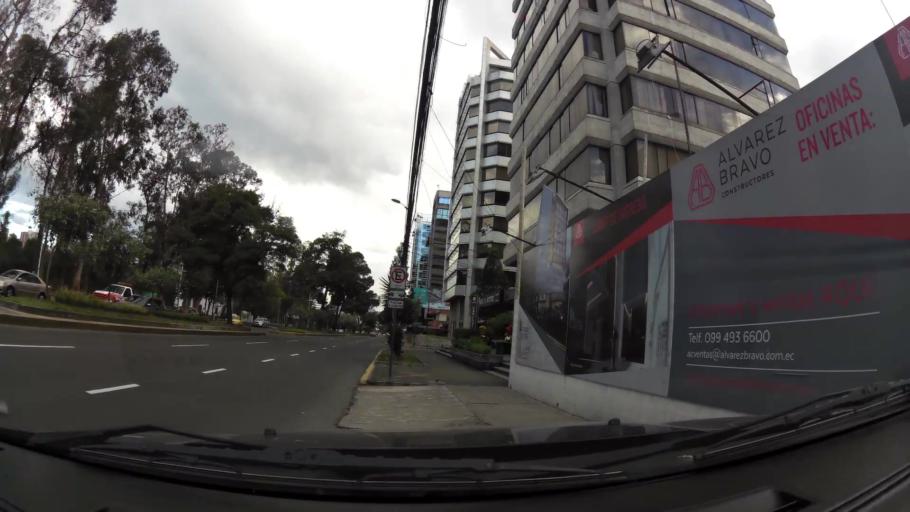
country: EC
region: Pichincha
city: Quito
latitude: -0.1841
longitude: -78.4871
